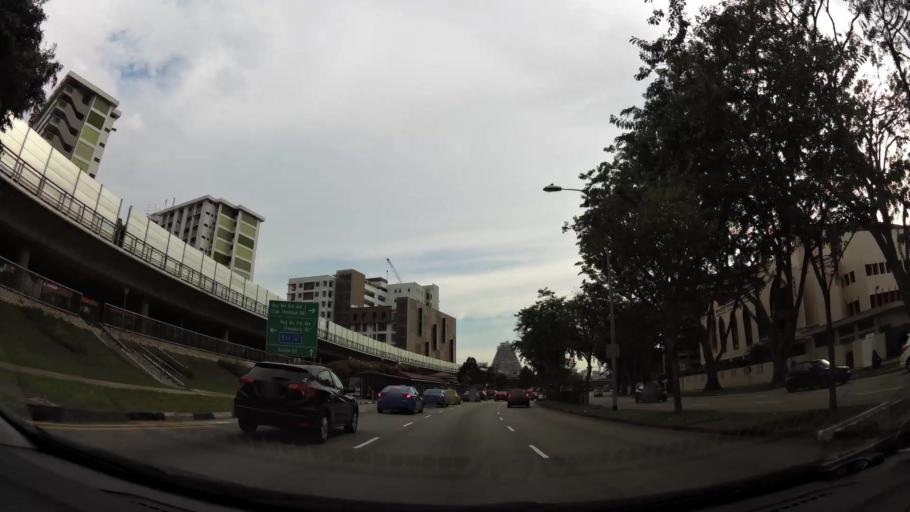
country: SG
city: Singapore
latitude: 1.3624
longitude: 103.8530
